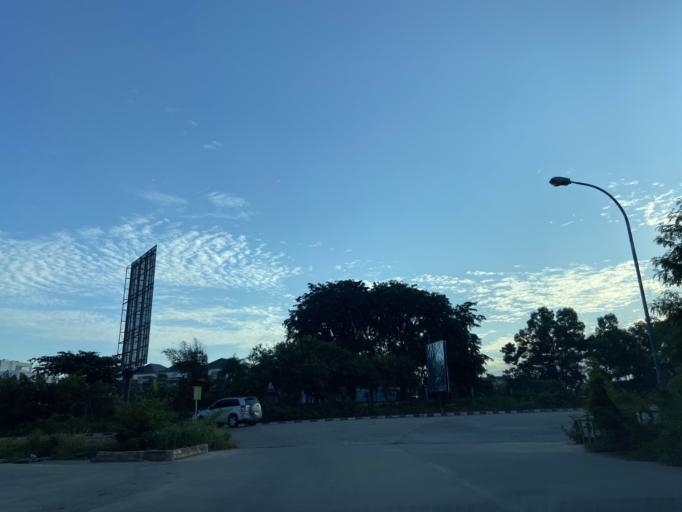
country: SG
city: Singapore
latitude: 1.1251
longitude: 104.0420
